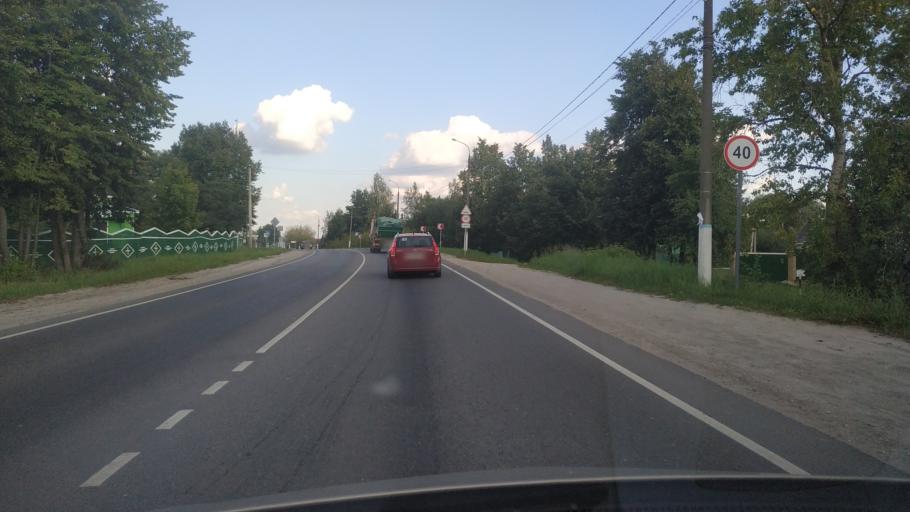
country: RU
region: Moskovskaya
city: Shatura
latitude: 55.5783
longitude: 39.4861
